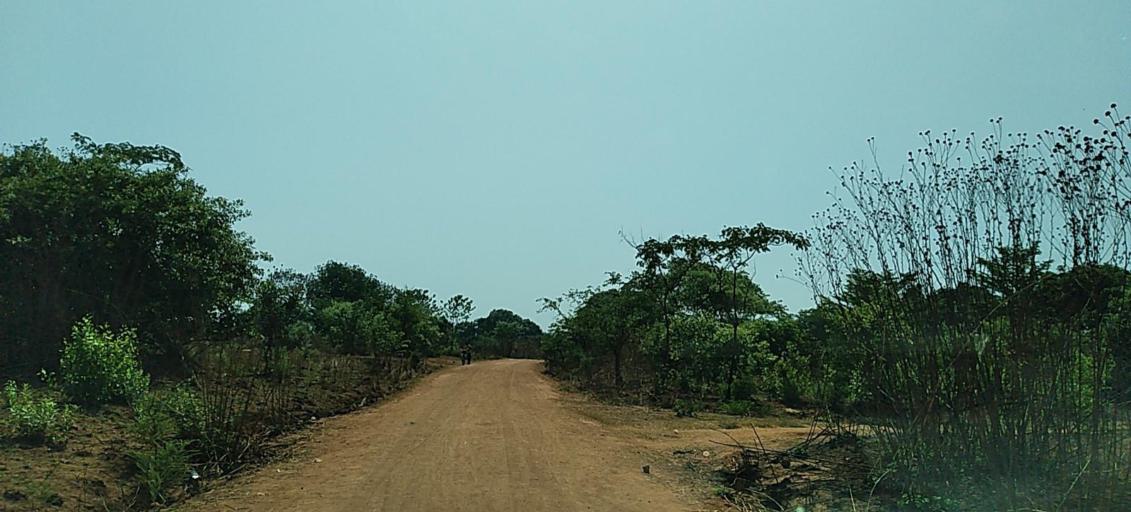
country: ZM
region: Copperbelt
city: Luanshya
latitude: -13.3484
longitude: 28.3966
